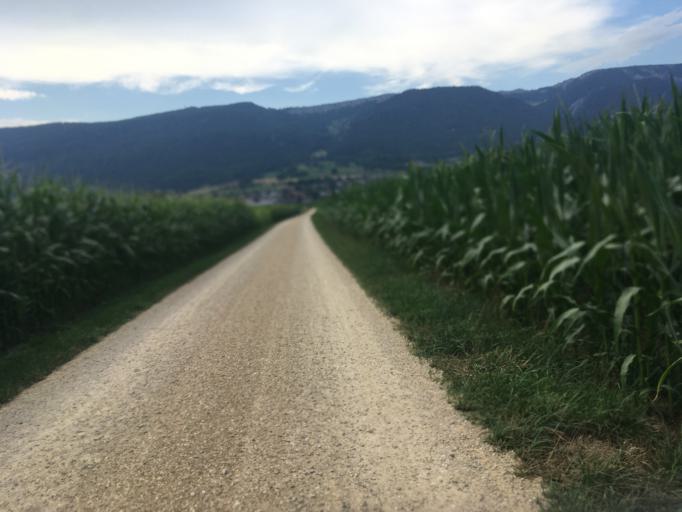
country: CH
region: Solothurn
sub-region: Bezirk Lebern
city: Bettlach
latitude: 47.1872
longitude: 7.4243
